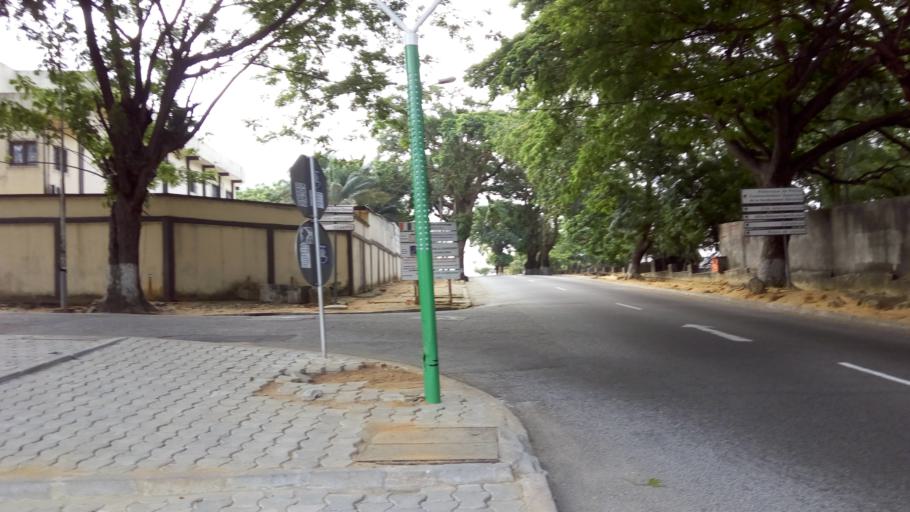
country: CI
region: Lagunes
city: Abidjan
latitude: 5.3295
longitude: -4.0197
